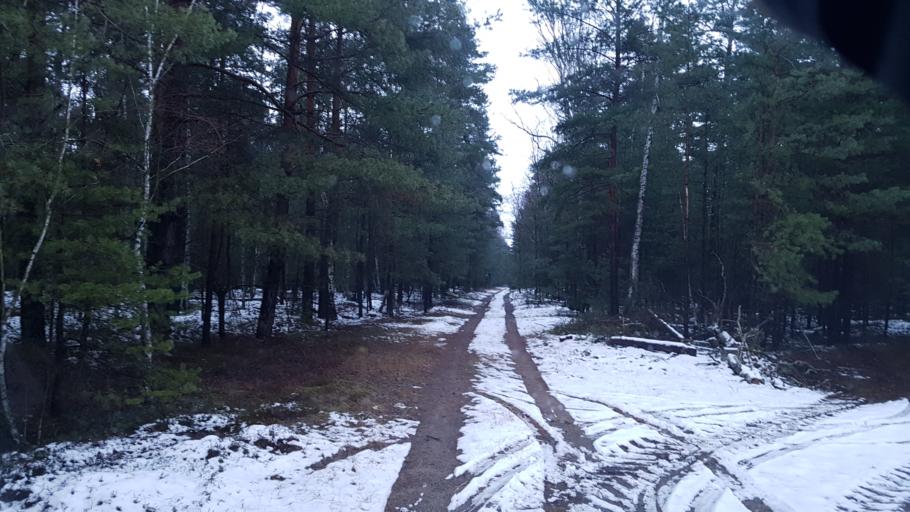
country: DE
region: Brandenburg
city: Janschwalde
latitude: 51.8848
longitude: 14.5652
